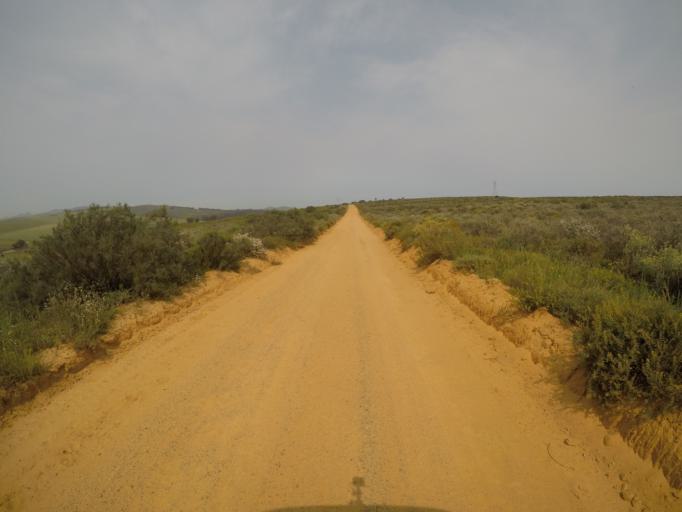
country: ZA
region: Western Cape
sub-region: West Coast District Municipality
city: Malmesbury
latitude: -33.4494
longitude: 18.7459
